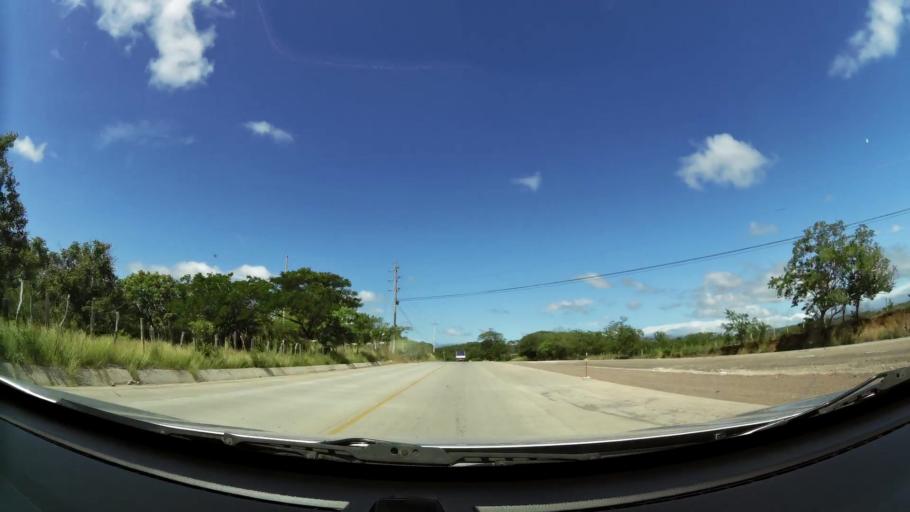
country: CR
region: Guanacaste
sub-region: Canton de Canas
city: Canas
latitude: 10.4378
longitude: -85.1070
